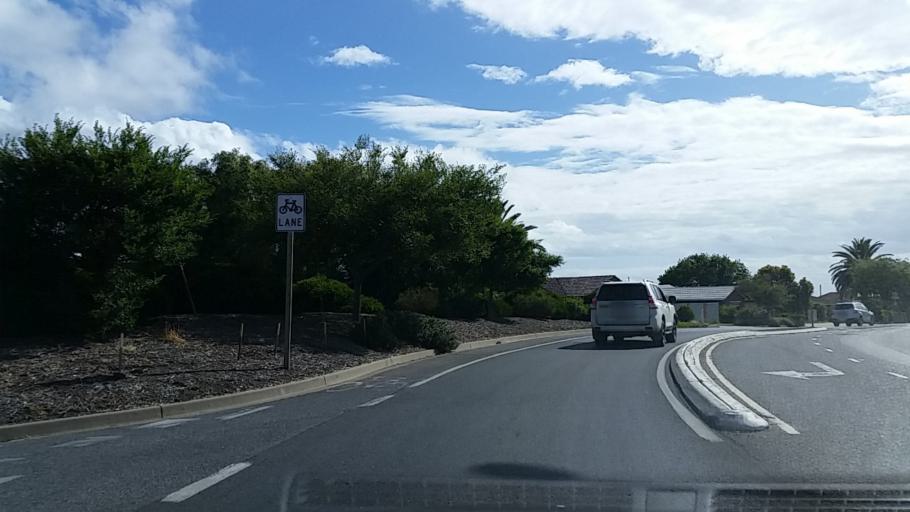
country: AU
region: South Australia
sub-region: Adelaide
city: Port Noarlunga
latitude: -35.1459
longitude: 138.4866
